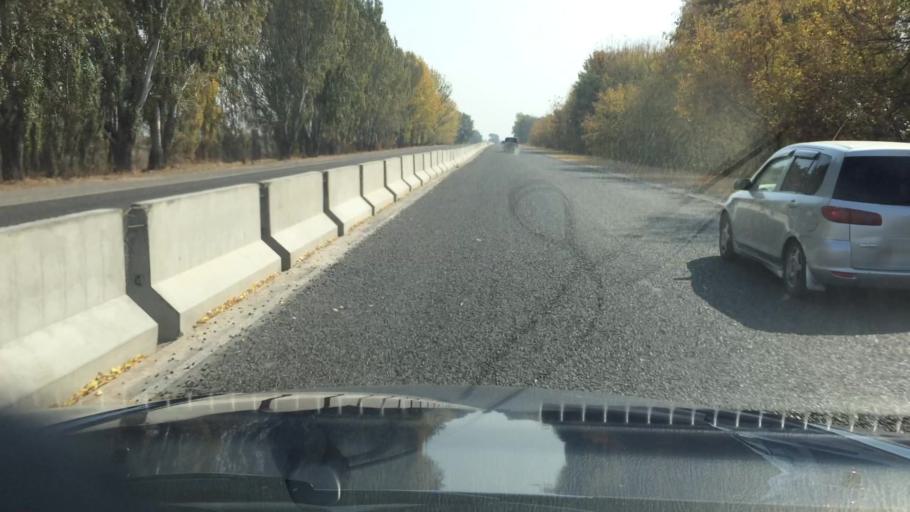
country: KG
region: Chuy
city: Kant
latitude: 42.9642
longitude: 74.9147
